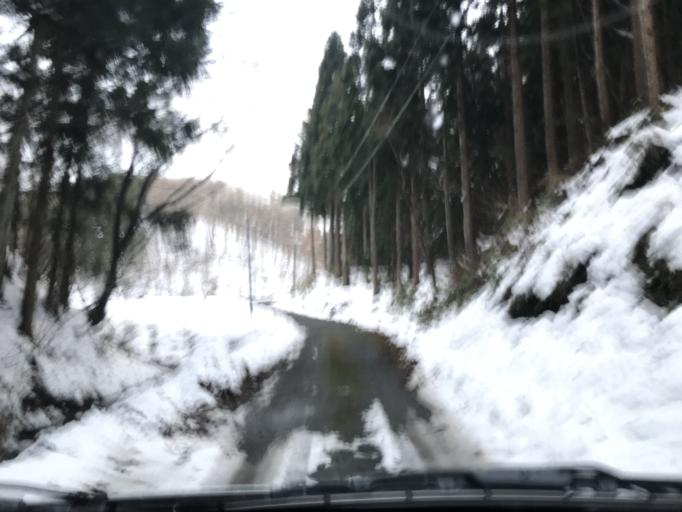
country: JP
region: Iwate
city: Mizusawa
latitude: 39.0385
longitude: 141.0085
